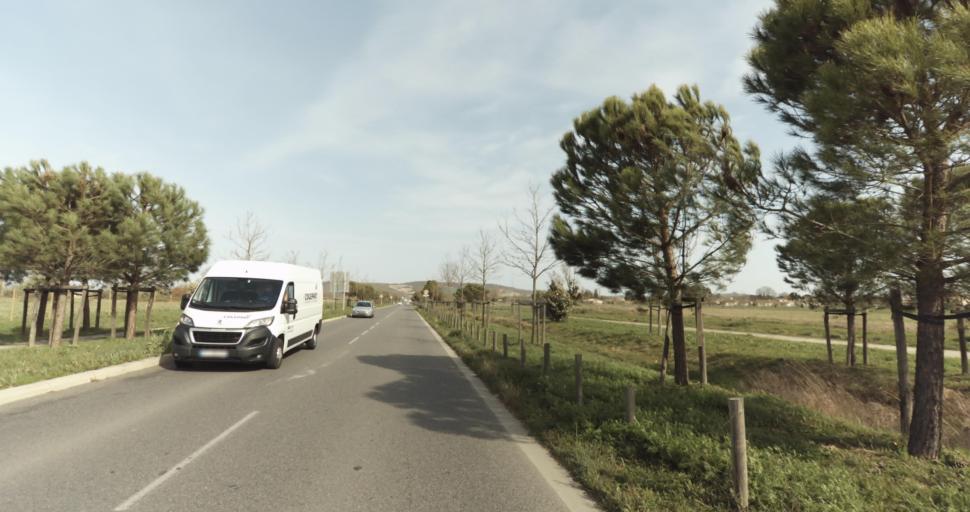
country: FR
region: Midi-Pyrenees
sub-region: Departement du Tarn
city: Saint-Sulpice-la-Pointe
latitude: 43.7581
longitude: 1.6587
